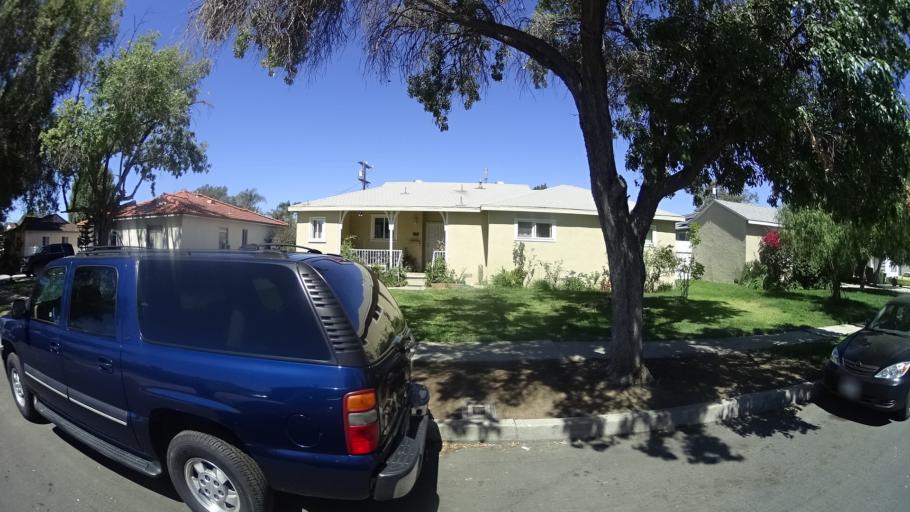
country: US
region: California
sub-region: Los Angeles County
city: San Fernando
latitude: 34.2548
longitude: -118.4640
